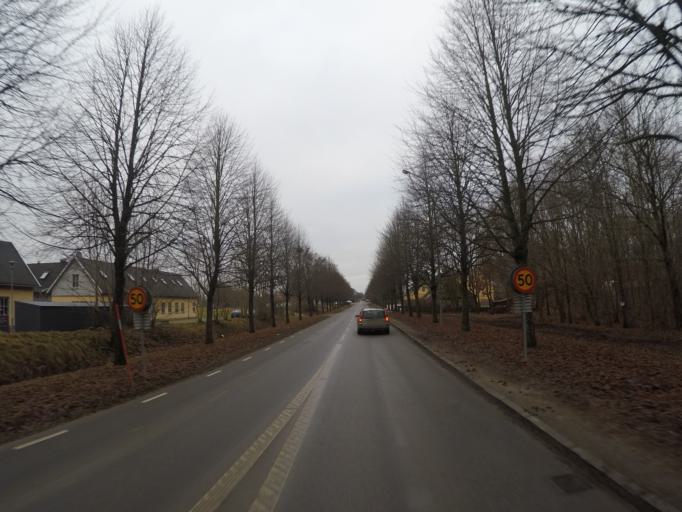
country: SE
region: Skane
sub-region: Eslovs Kommun
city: Eslov
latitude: 55.7460
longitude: 13.3524
